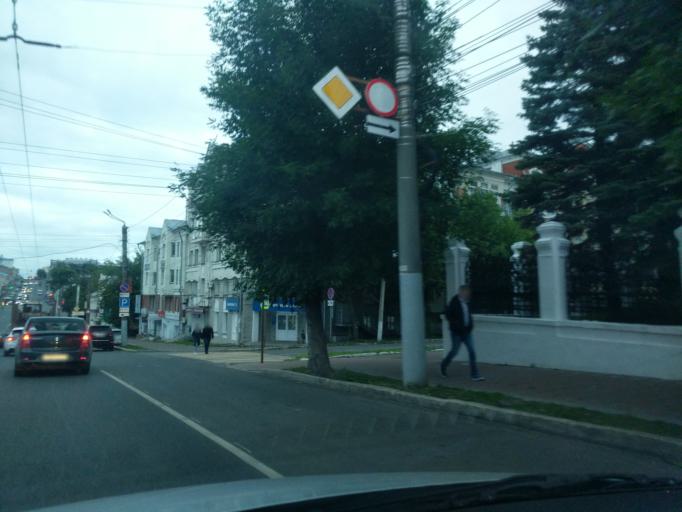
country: RU
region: Kirov
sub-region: Kirovo-Chepetskiy Rayon
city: Kirov
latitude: 58.5985
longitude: 49.6815
